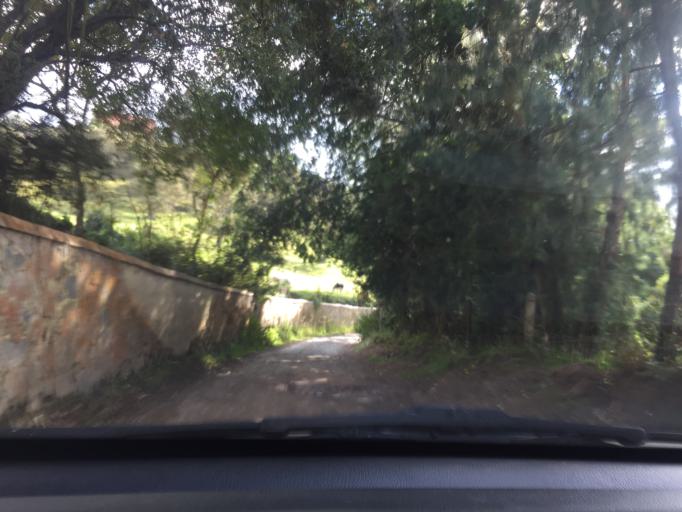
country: CO
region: Cundinamarca
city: Sopo
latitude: 4.9199
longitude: -73.9137
